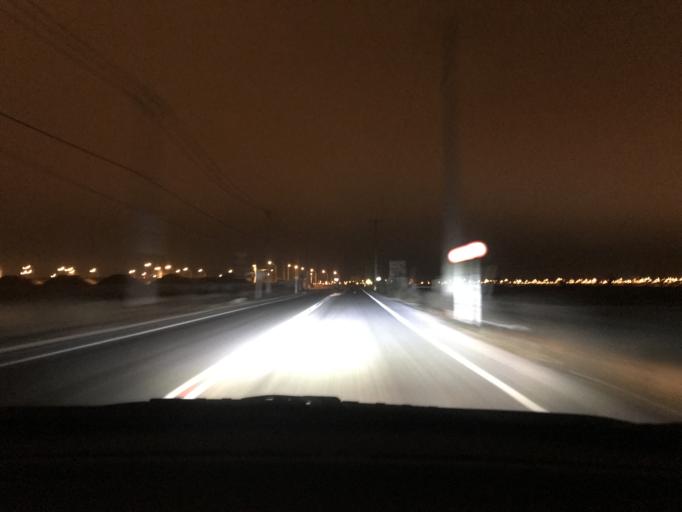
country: CL
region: Coquimbo
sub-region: Provincia de Elqui
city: La Serena
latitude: -29.9230
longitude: -71.2259
